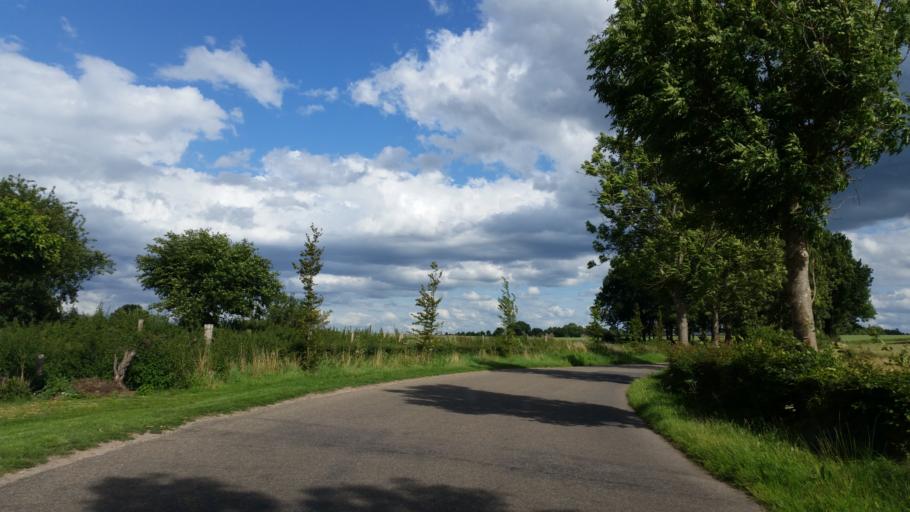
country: NL
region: Limburg
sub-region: Eijsden-Margraten
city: Margraten
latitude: 50.7898
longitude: 5.8175
